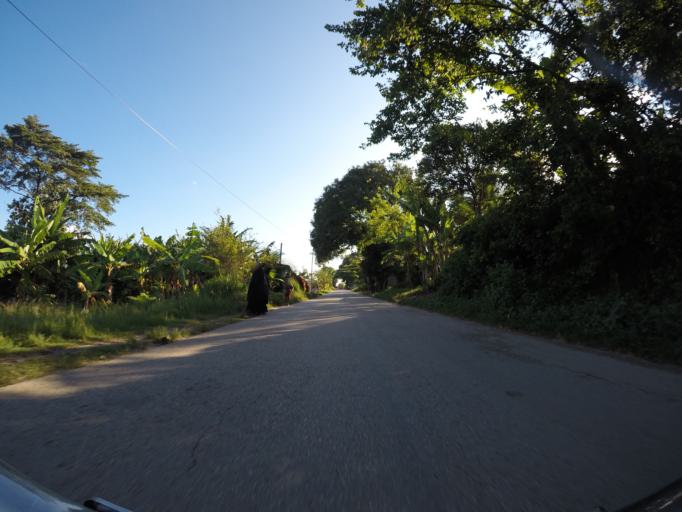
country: TZ
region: Pemba South
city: Chake Chake
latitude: -5.3190
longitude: 39.7429
